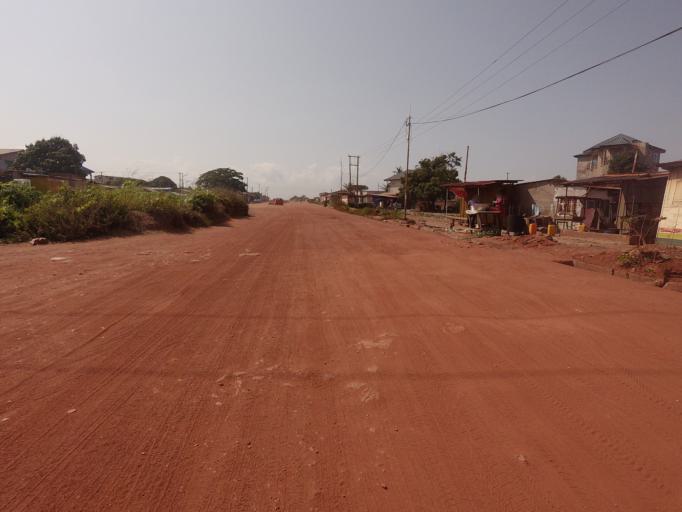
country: GH
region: Greater Accra
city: Teshi Old Town
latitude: 5.5794
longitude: -0.1123
